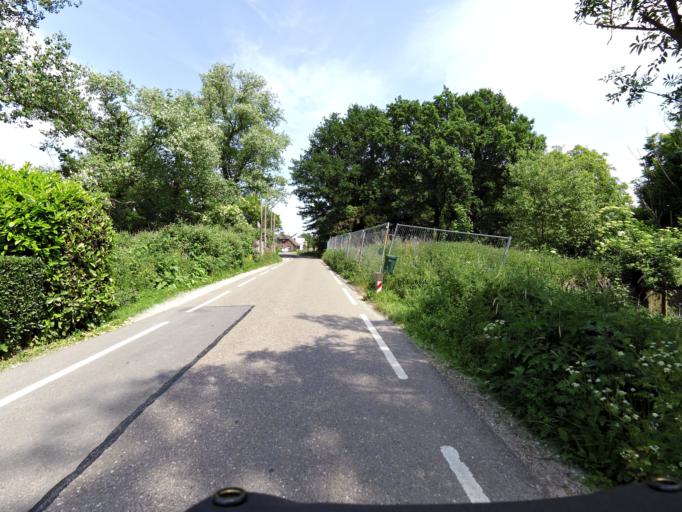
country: NL
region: North Brabant
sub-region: Gemeente Woudrichem
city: Woudrichem
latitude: 51.7950
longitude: 5.0548
